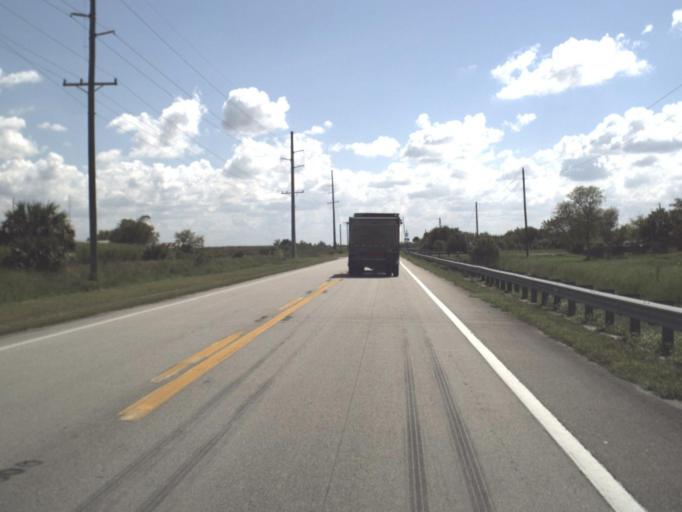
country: US
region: Florida
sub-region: Glades County
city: Moore Haven
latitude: 26.8542
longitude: -81.1228
